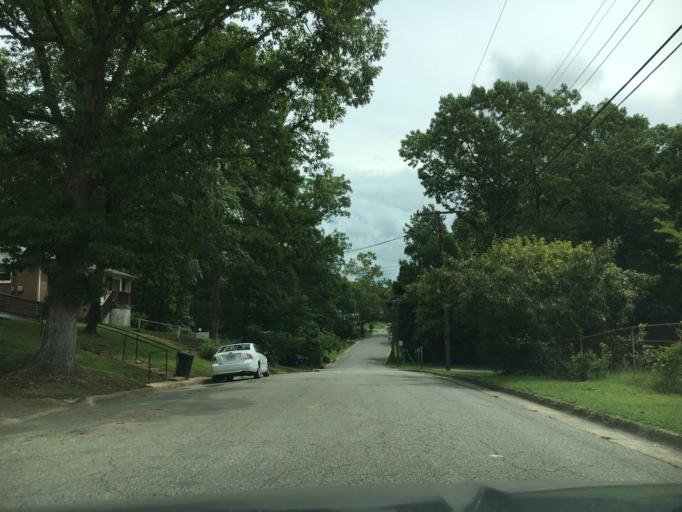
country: US
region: Virginia
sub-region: Halifax County
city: South Boston
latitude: 36.7075
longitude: -78.9061
